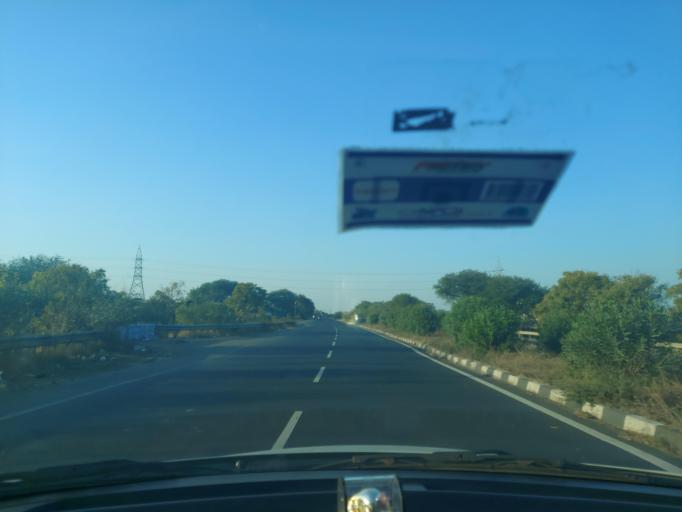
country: IN
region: Madhya Pradesh
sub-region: Indore
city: Sanwer
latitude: 23.0550
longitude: 75.8254
